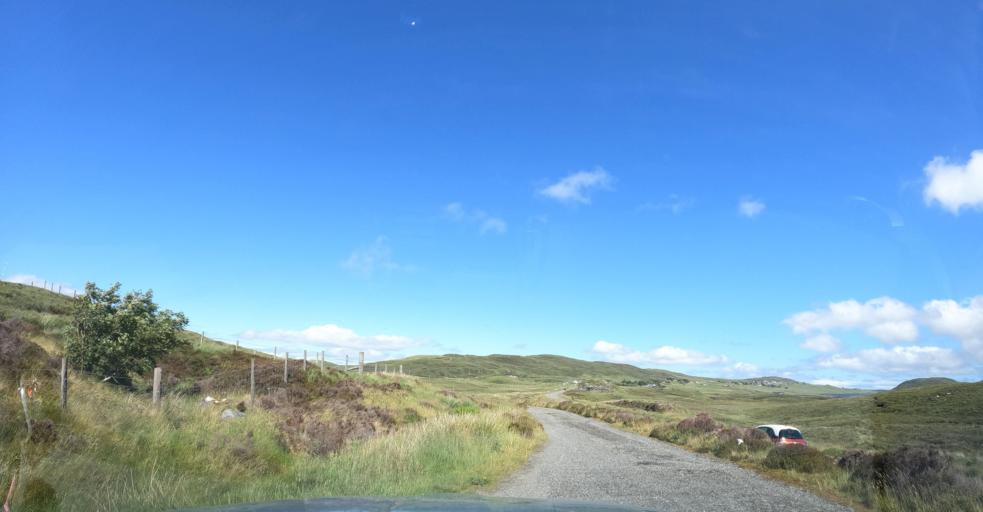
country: GB
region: Scotland
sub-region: Eilean Siar
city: Harris
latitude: 58.0799
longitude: -6.6481
